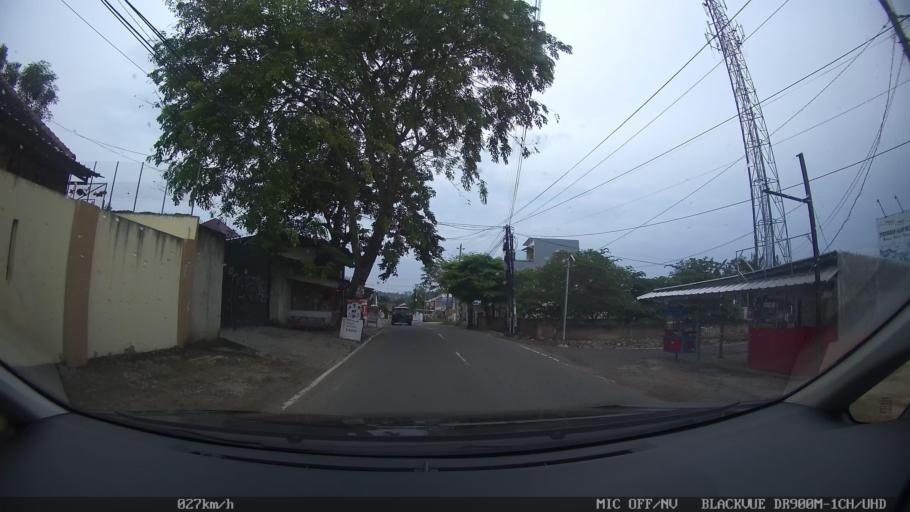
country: ID
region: Lampung
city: Kedaton
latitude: -5.3795
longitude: 105.2380
